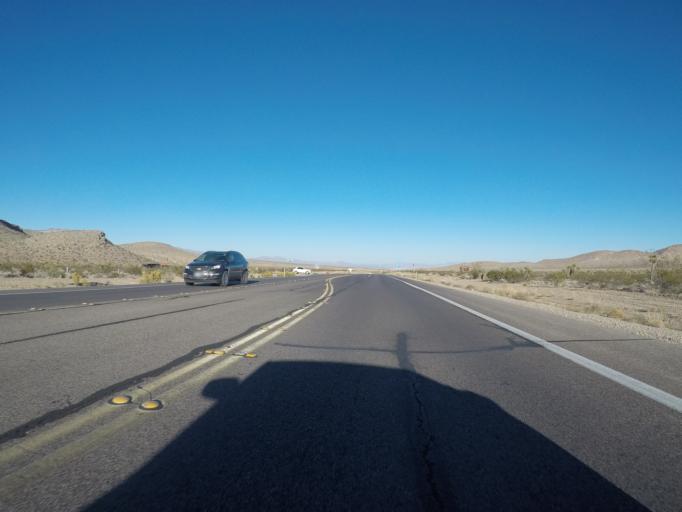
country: US
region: Nevada
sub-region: Clark County
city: Summerlin South
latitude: 36.1411
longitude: -115.4005
